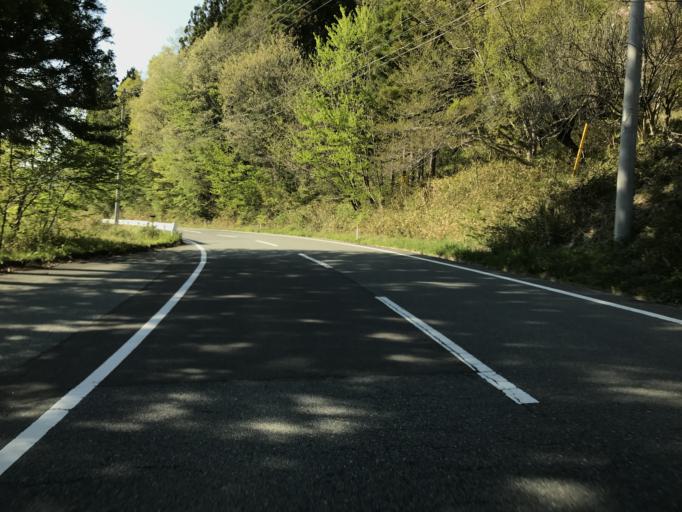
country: JP
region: Fukushima
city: Funehikimachi-funehiki
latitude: 37.5099
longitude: 140.7606
